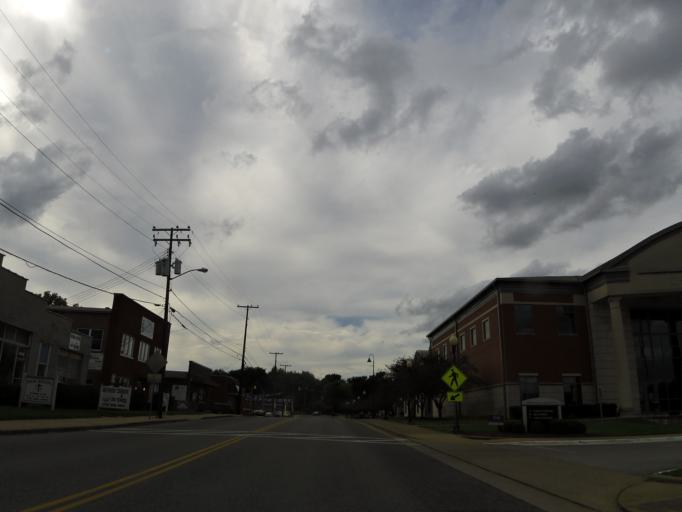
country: US
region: Kentucky
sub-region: Christian County
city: Hopkinsville
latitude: 36.8666
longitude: -87.4915
